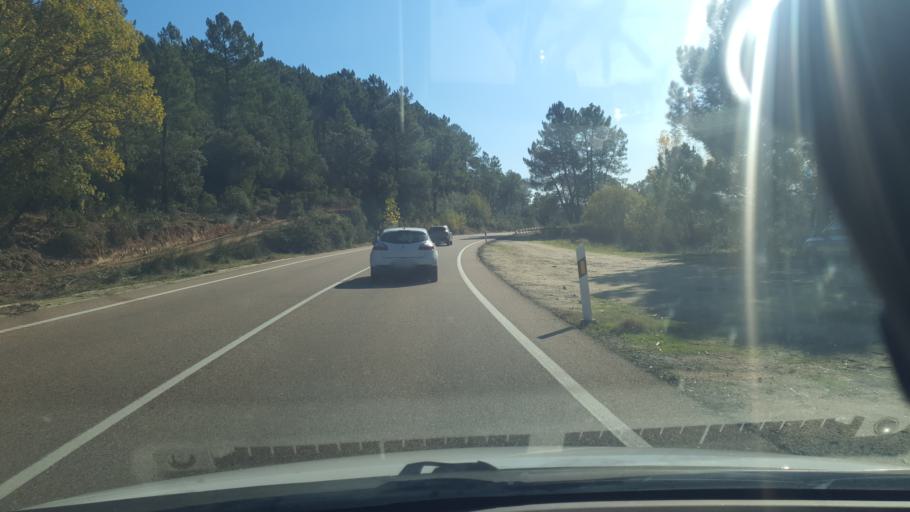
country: ES
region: Castille and Leon
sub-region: Provincia de Avila
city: Poyales del Hoyo
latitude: 40.1676
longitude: -5.1224
